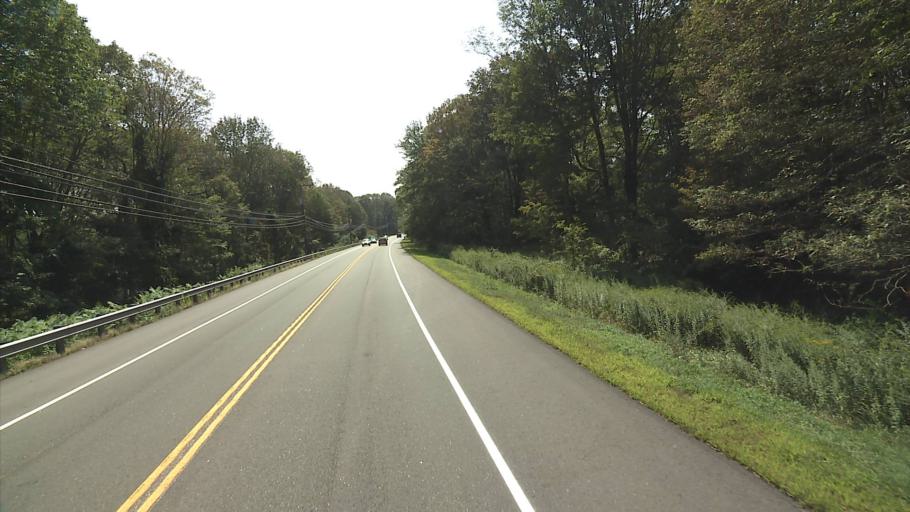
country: US
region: Connecticut
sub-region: New Haven County
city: Madison Center
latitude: 41.3505
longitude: -72.6329
